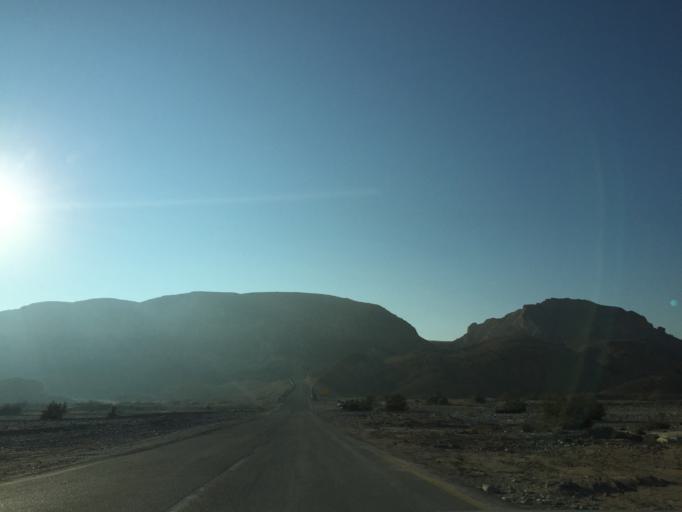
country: IL
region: Southern District
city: Mitzpe Ramon
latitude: 30.3260
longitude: 34.9551
